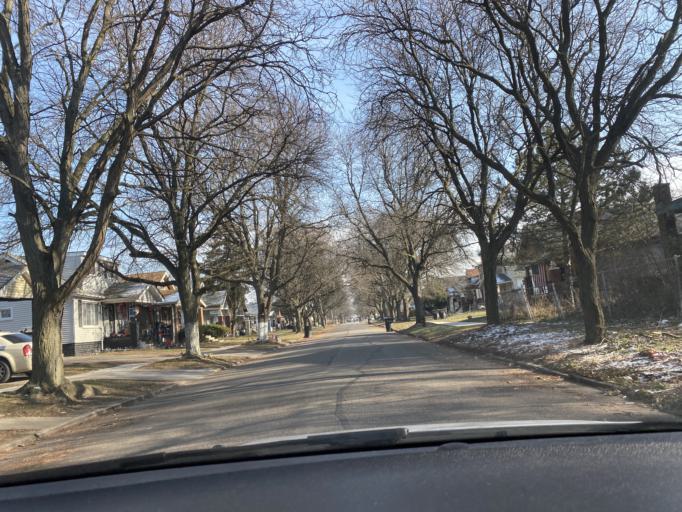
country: US
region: Michigan
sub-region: Wayne County
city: Highland Park
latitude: 42.3742
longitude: -83.1436
